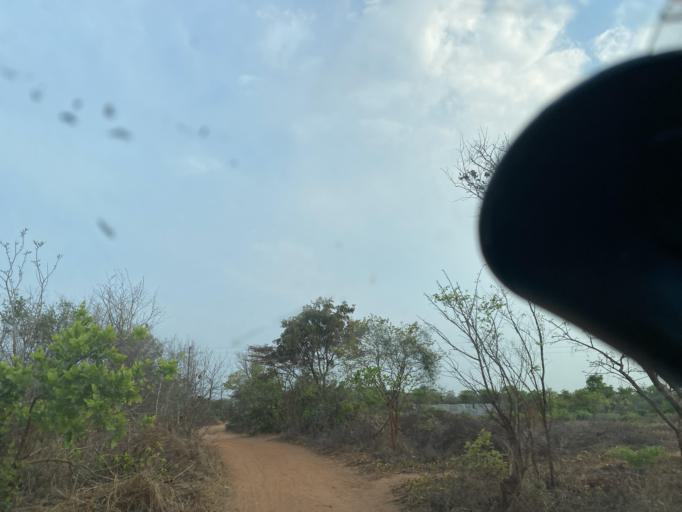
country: ZM
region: Lusaka
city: Chongwe
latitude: -15.1975
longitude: 28.4934
